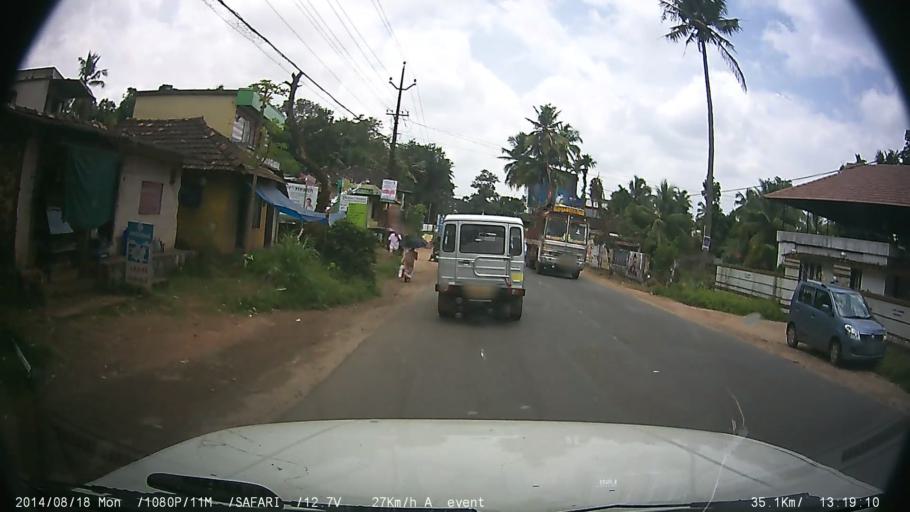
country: IN
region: Kerala
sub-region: Kottayam
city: Kottayam
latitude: 9.6080
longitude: 76.5320
